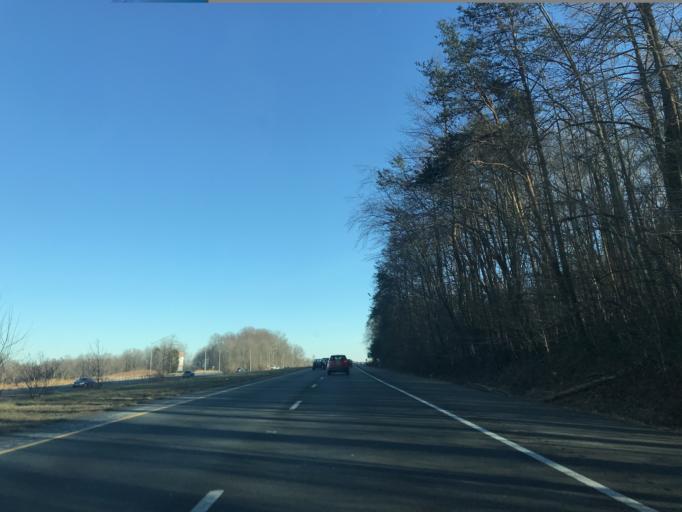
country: US
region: Maryland
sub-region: Prince George's County
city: Mellwood
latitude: 38.8159
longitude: -76.8322
